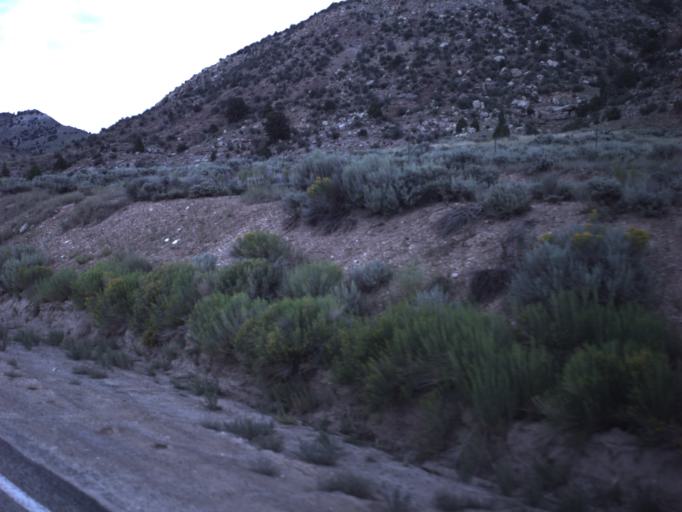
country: US
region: Utah
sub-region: Carbon County
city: Helper
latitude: 39.8246
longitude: -110.7864
